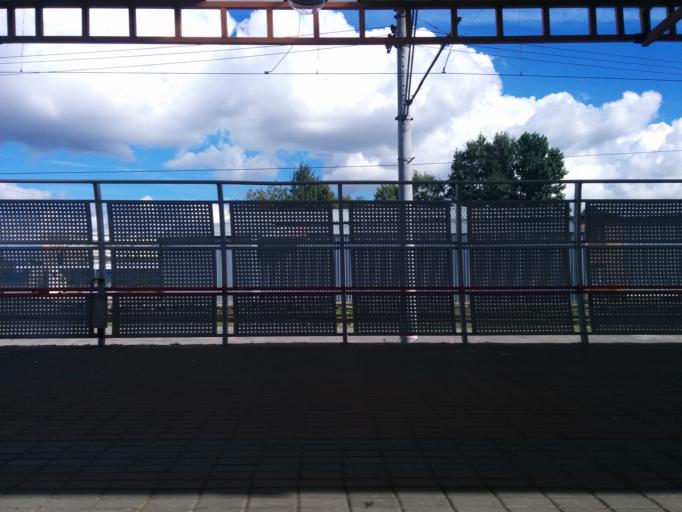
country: RU
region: Moscow
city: Mar'ina Roshcha
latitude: 55.7956
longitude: 37.5893
